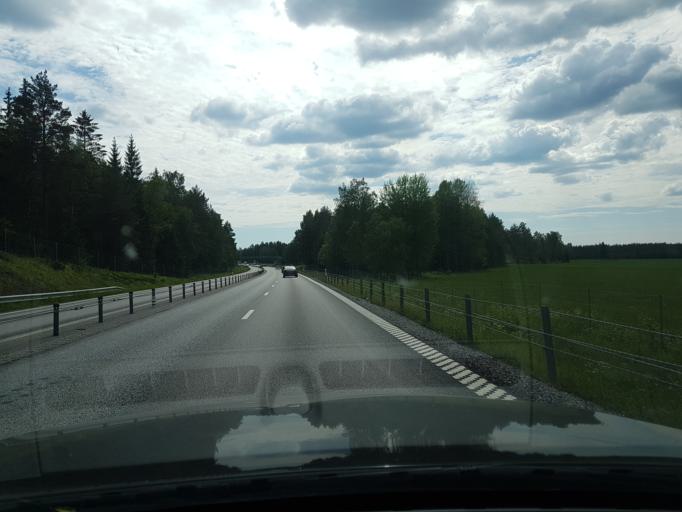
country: SE
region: Stockholm
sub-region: Osterakers Kommun
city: Akersberga
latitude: 59.6123
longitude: 18.2849
